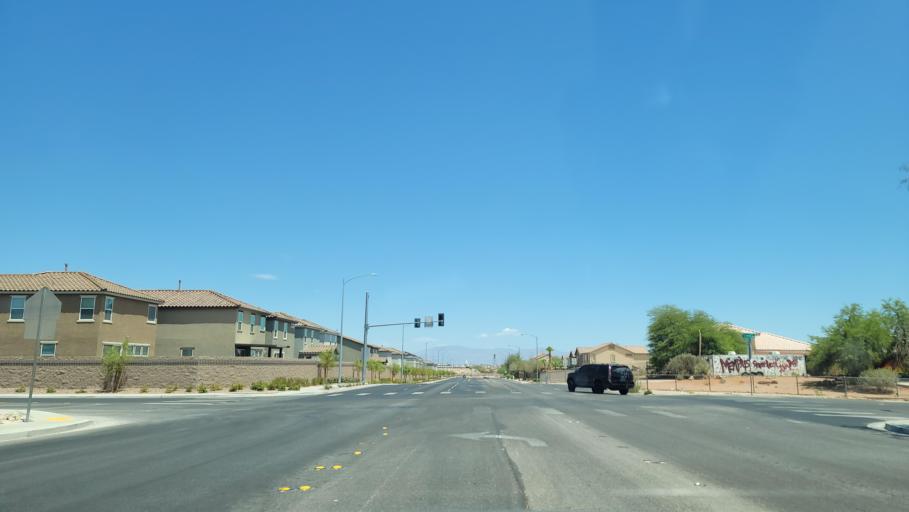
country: US
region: Nevada
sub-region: Clark County
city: Enterprise
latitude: 35.9946
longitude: -115.2346
